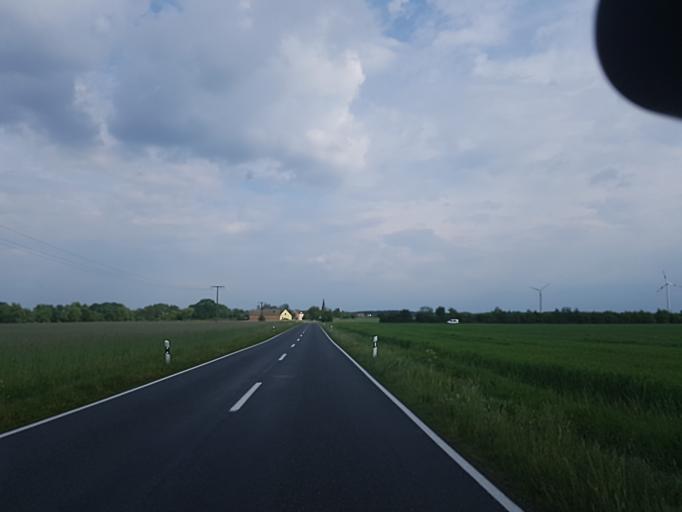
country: DE
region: Saxony-Anhalt
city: Klieken
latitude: 51.9167
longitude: 12.4032
